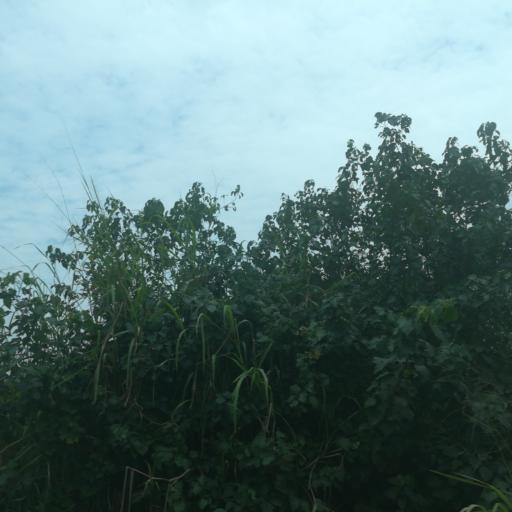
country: NG
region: Lagos
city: Ejirin
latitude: 6.6658
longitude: 3.7932
